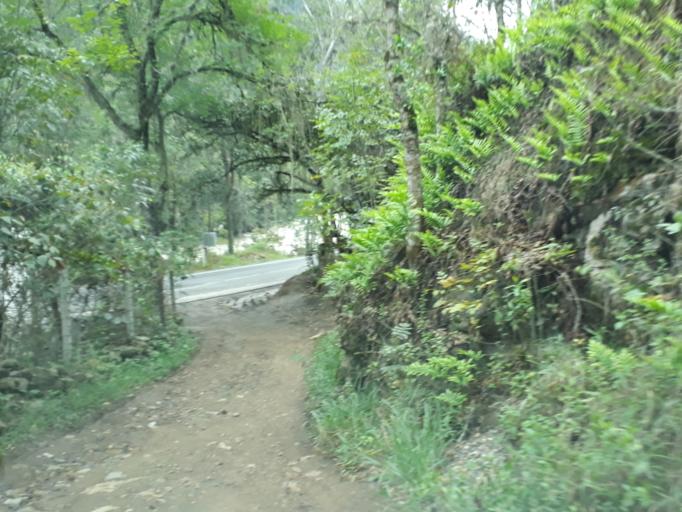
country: CO
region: Cundinamarca
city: Manta
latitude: 5.0617
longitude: -73.5266
